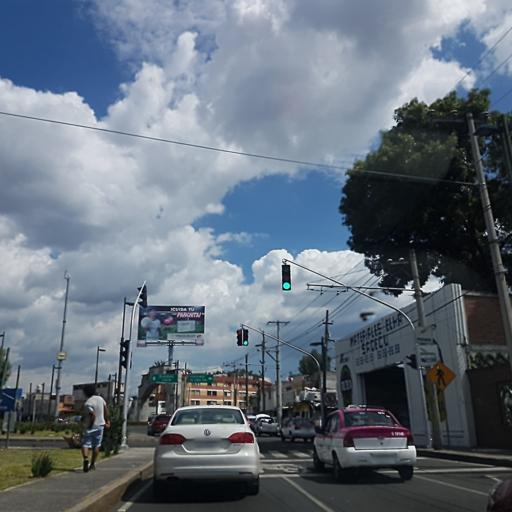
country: MX
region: Mexico City
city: Iztapalapa
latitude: 19.3297
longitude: -99.1072
